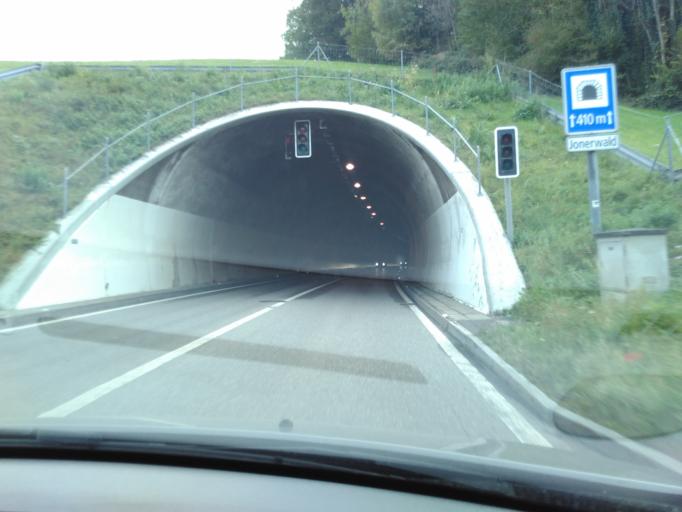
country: CH
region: Zurich
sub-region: Bezirk Hinwil
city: Rueti / Dorfzentrum, Suedl. Teil
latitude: 47.2384
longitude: 8.8649
